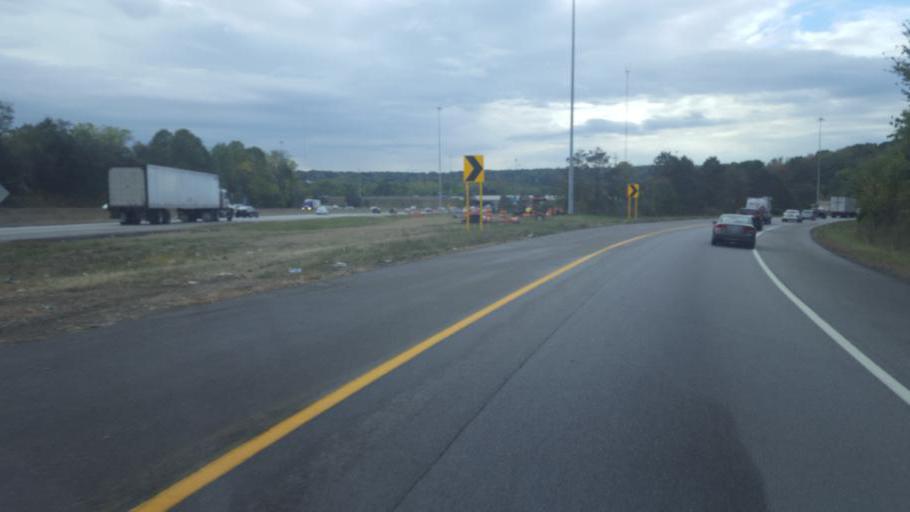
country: US
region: Ohio
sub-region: Summit County
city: Akron
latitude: 41.0602
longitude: -81.5624
